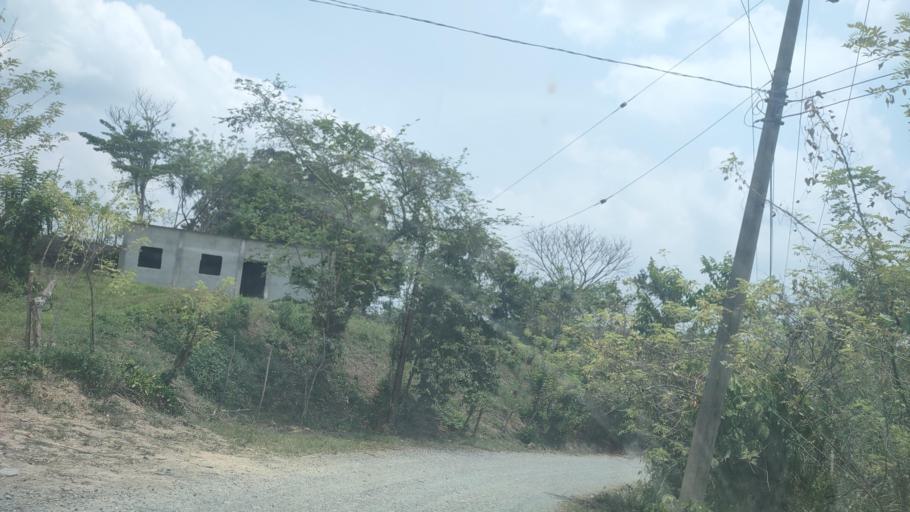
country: MX
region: Tabasco
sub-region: Huimanguillo
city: Francisco Rueda
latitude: 17.5899
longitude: -93.9582
